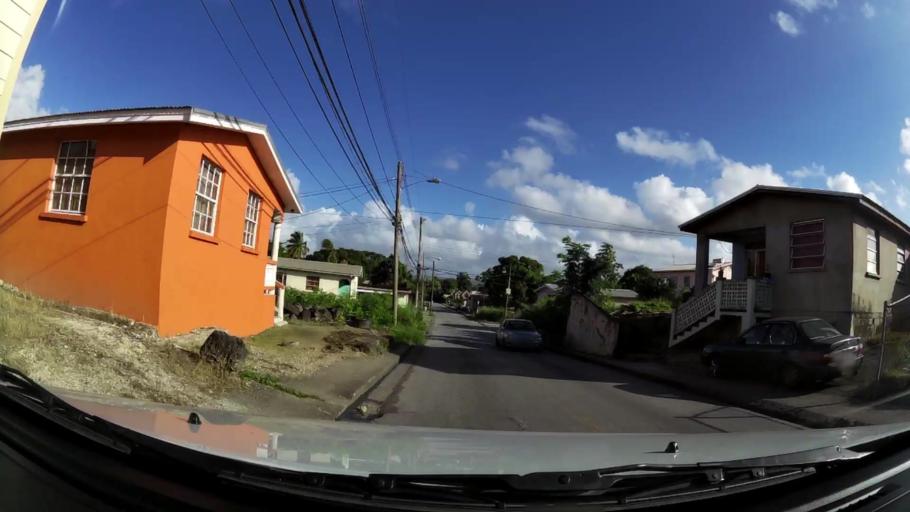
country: BB
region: Saint Michael
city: Bridgetown
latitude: 13.1068
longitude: -59.5896
